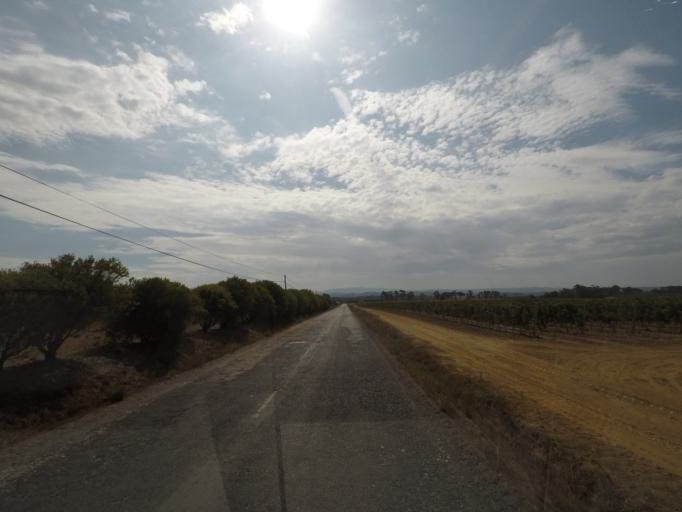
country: PT
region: Beja
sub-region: Odemira
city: Sao Teotonio
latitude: 37.4704
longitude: -8.7544
